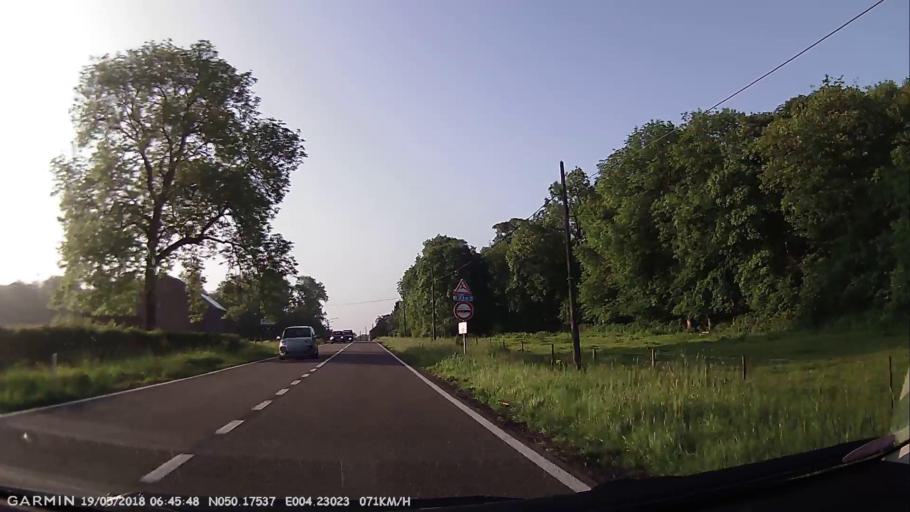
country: BE
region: Wallonia
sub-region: Province du Hainaut
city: Beaumont
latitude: 50.1752
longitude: 4.2305
